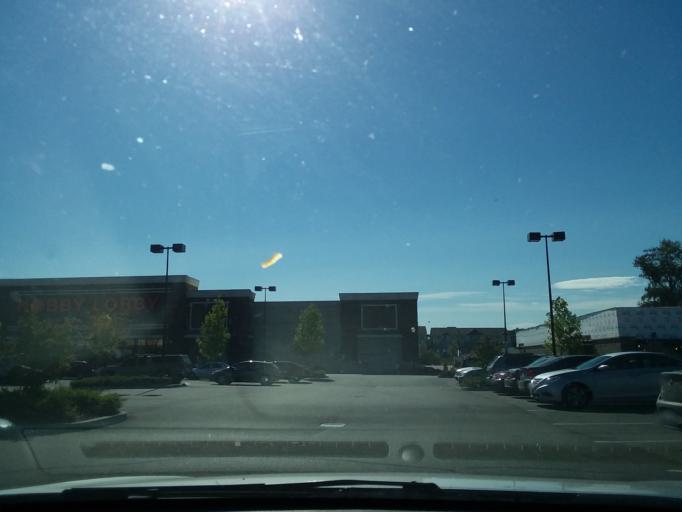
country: US
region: Washington
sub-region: Snohomish County
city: Smokey Point
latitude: 48.1530
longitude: -122.1970
